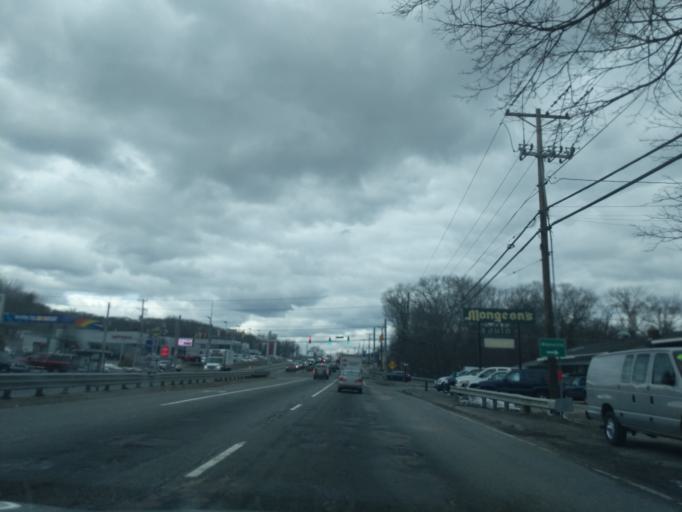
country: US
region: Rhode Island
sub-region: Providence County
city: Cumberland Hill
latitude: 41.9598
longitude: -71.4932
